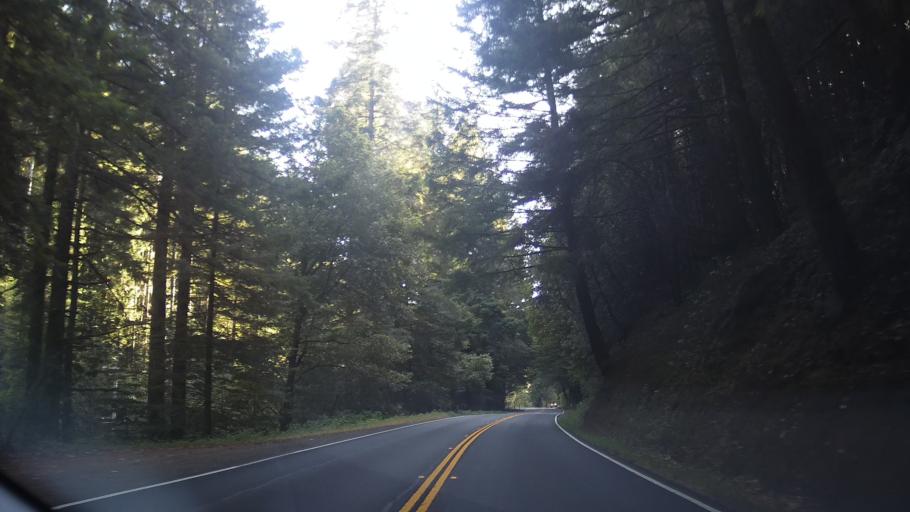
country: US
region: California
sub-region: Mendocino County
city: Brooktrails
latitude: 39.3486
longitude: -123.5893
